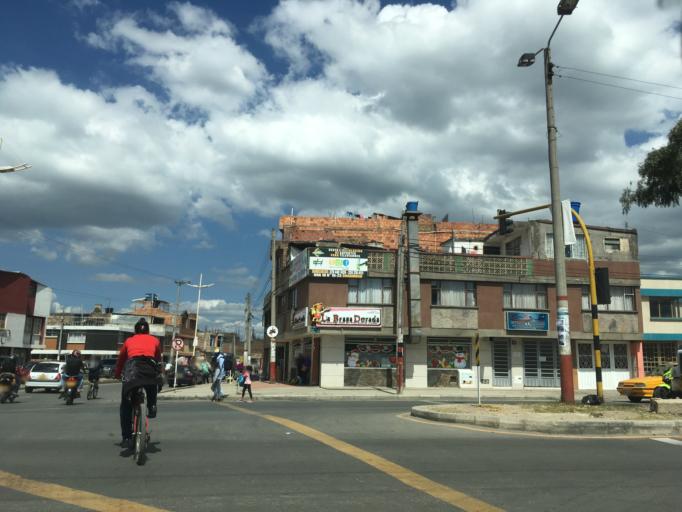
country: CO
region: Boyaca
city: Sogamoso
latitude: 5.7107
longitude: -72.9320
